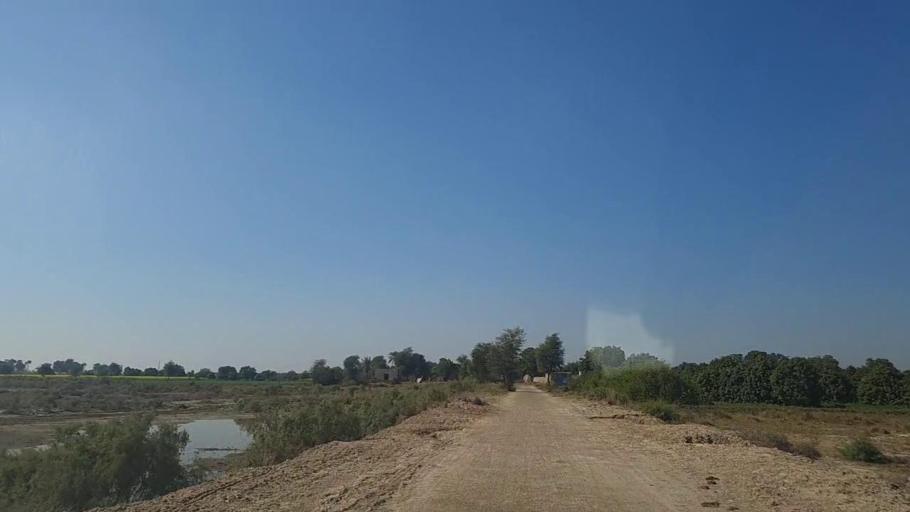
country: PK
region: Sindh
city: Sinjhoro
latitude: 26.1540
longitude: 68.8596
